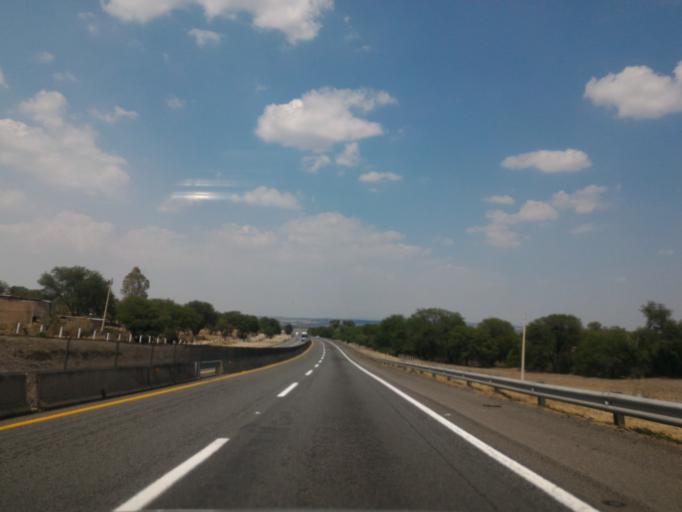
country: MX
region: Jalisco
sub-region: San Juan de los Lagos
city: Mezquitic de la Magdalena
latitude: 21.2040
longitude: -102.3332
